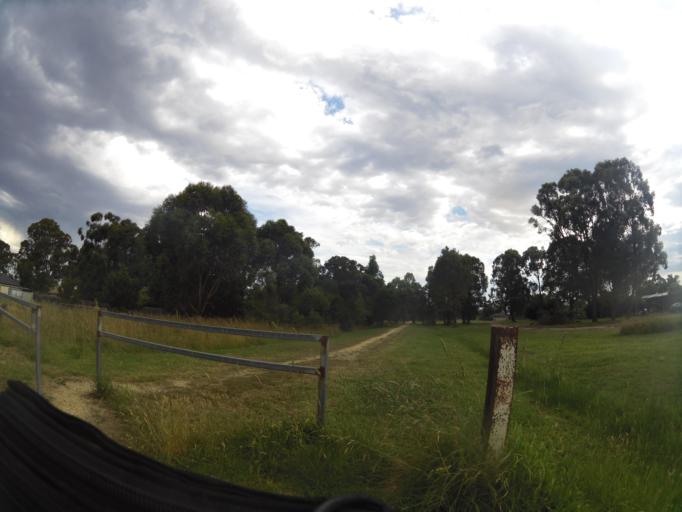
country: AU
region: Victoria
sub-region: Latrobe
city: Traralgon
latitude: -38.0538
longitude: 146.6279
